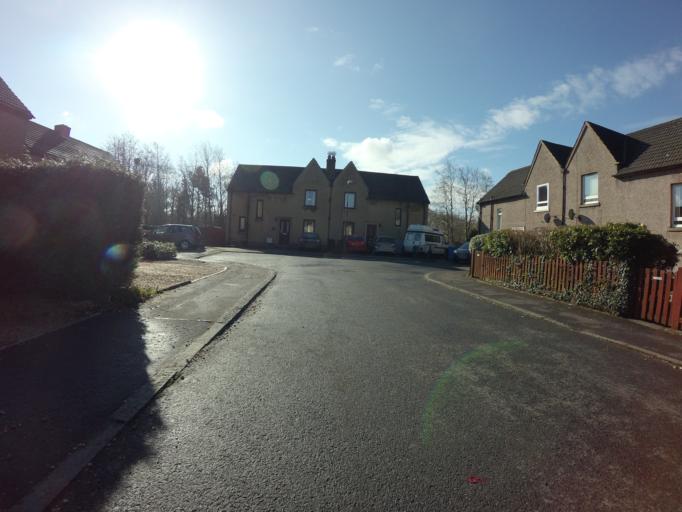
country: GB
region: Scotland
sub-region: West Lothian
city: Livingston
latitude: 55.8856
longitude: -3.5372
